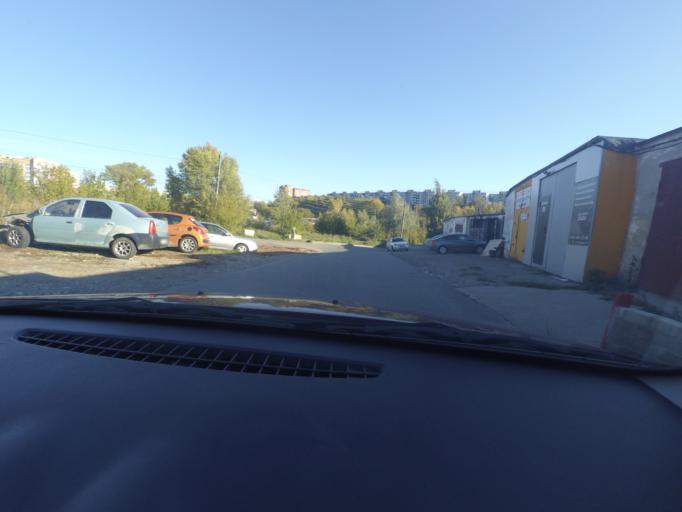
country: RU
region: Nizjnij Novgorod
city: Afonino
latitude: 56.3012
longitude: 44.0674
